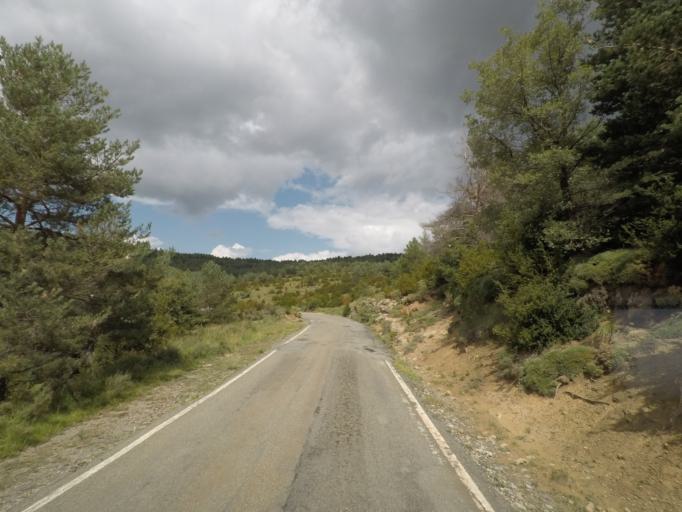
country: ES
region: Aragon
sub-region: Provincia de Huesca
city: Boltana
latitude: 42.4022
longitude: -0.0131
